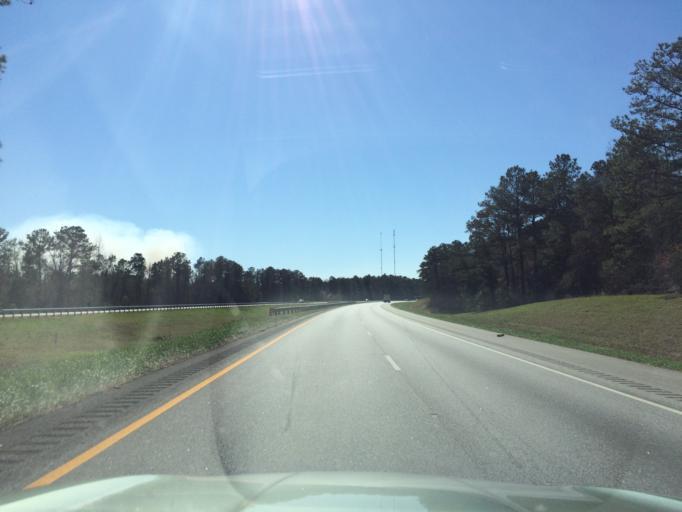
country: US
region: Alabama
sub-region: Lee County
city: Auburn
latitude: 32.5188
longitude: -85.5785
